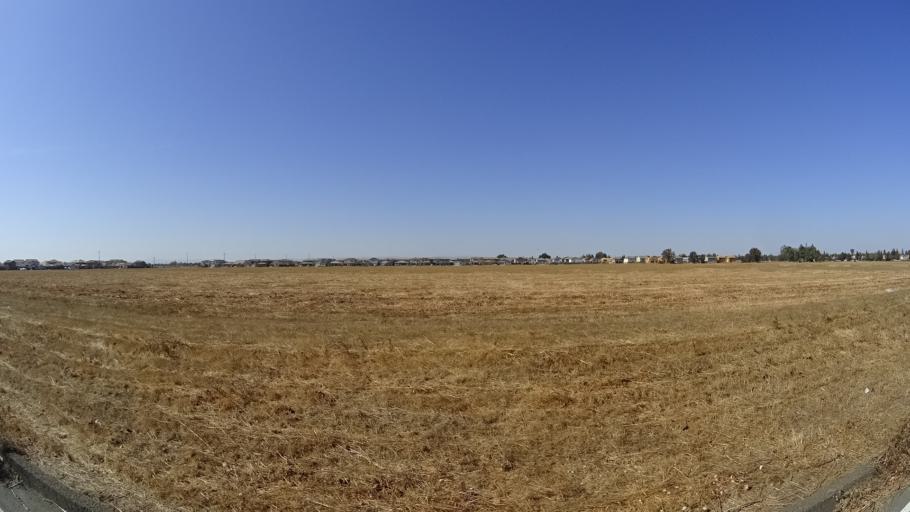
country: US
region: California
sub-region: Yolo County
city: Woodland
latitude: 38.6584
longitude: -121.7427
